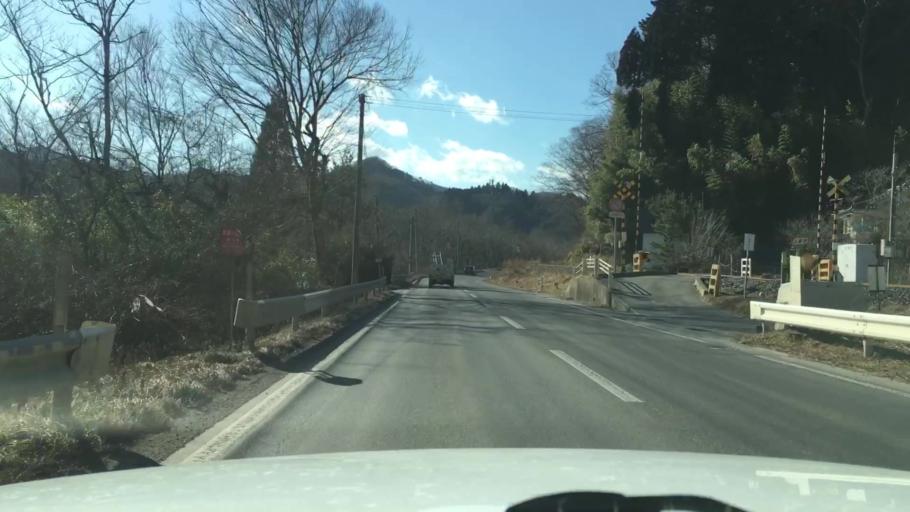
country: JP
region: Iwate
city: Miyako
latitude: 39.6319
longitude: 141.8795
